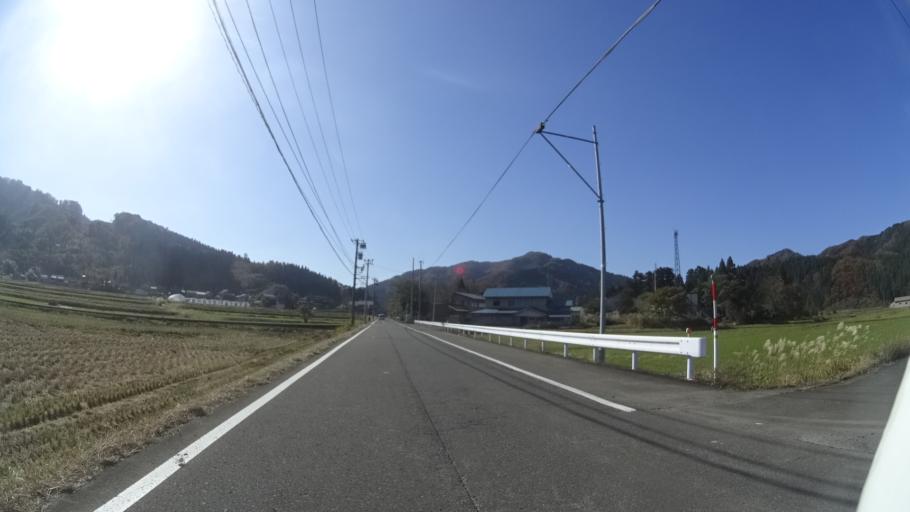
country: JP
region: Fukui
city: Sabae
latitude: 35.8839
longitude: 136.3395
